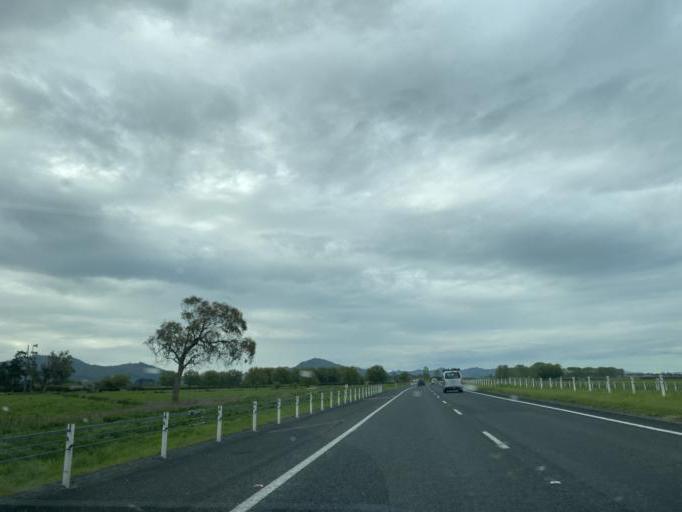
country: NZ
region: Waikato
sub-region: Waikato District
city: Ngaruawahia
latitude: -37.6599
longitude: 175.2058
